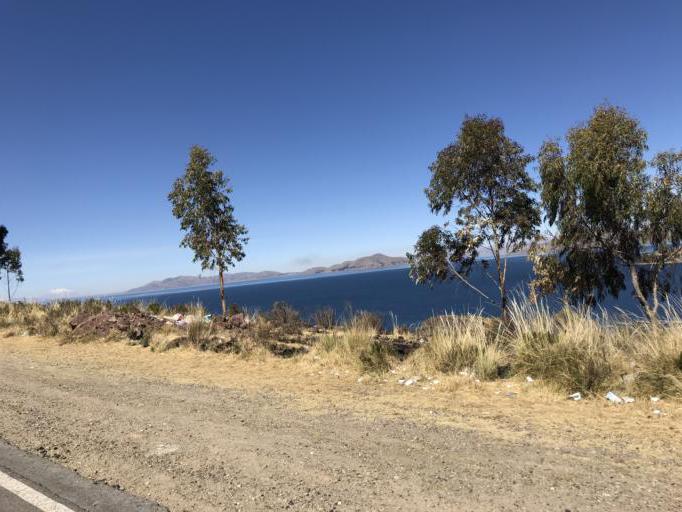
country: BO
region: La Paz
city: San Pablo
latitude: -16.2187
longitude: -68.8350
